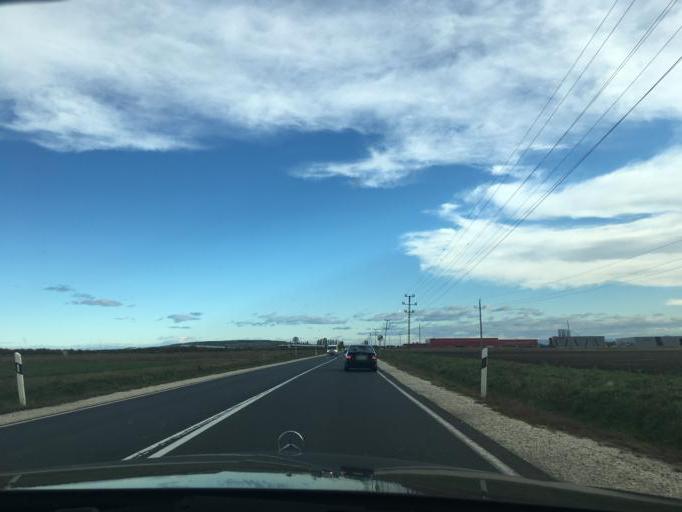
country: HU
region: Borsod-Abauj-Zemplen
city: Szikszo
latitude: 48.1684
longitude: 20.9094
